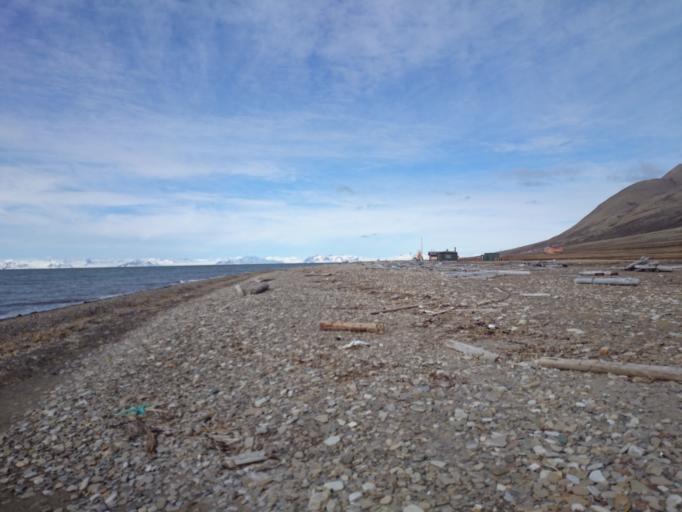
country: SJ
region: Svalbard
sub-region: Spitsbergen
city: Longyearbyen
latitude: 78.2501
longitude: 15.6796
